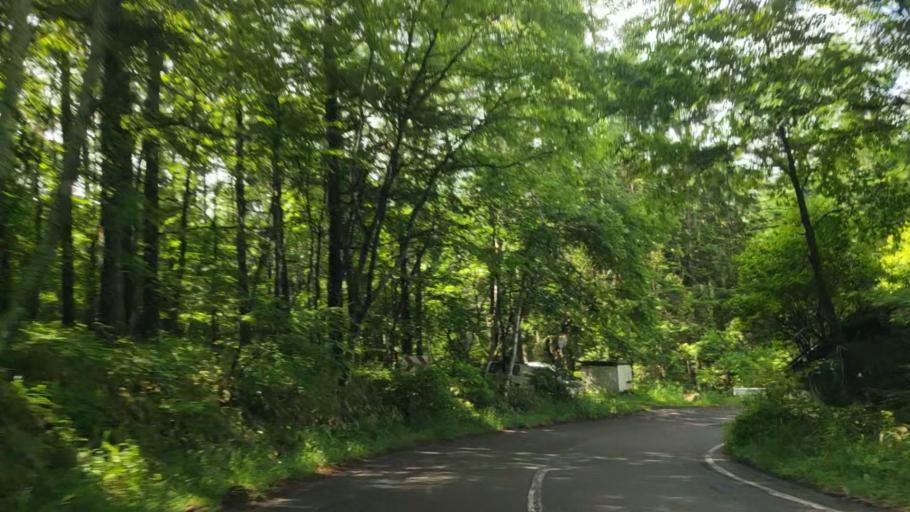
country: JP
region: Nagano
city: Suwa
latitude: 36.0878
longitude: 138.1477
